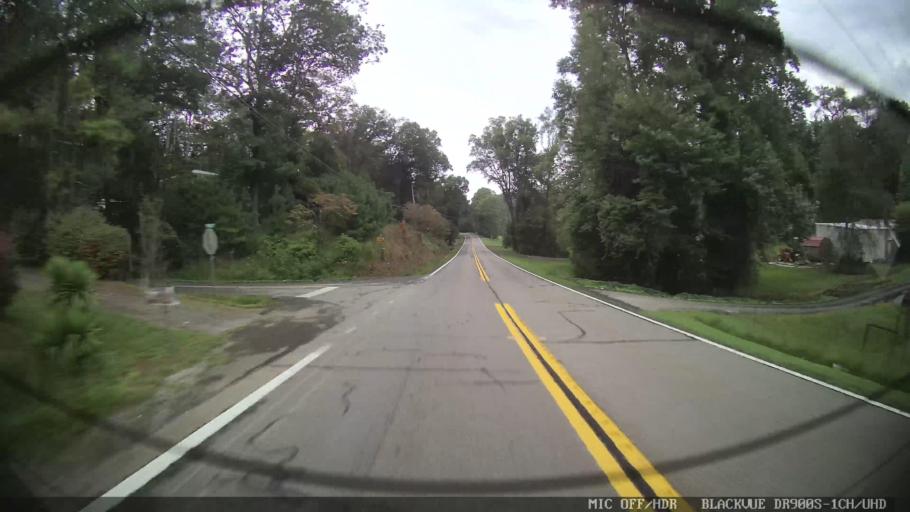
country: US
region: Georgia
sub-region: Gilmer County
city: Ellijay
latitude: 34.7125
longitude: -84.4991
